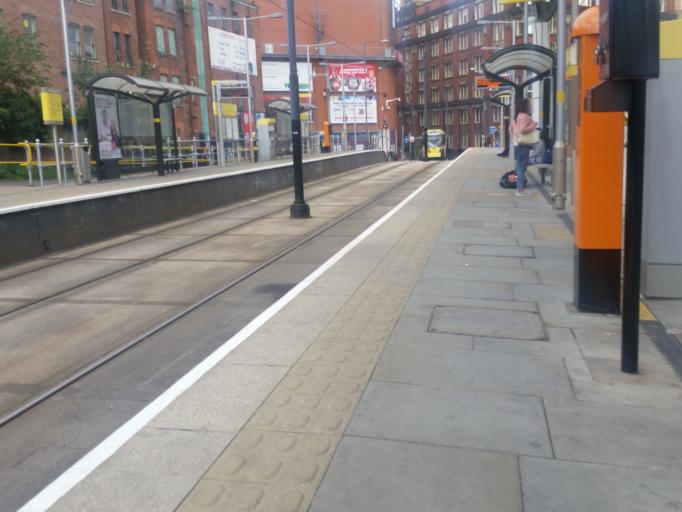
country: GB
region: England
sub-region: Manchester
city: Manchester
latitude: 53.4851
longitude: -2.2388
